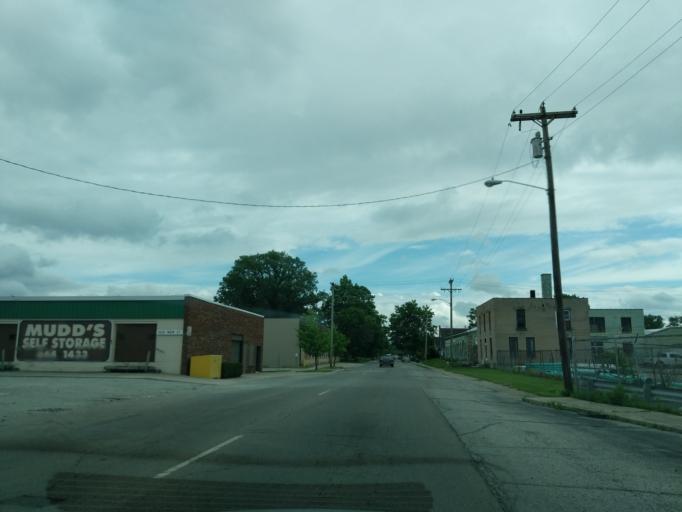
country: US
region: Indiana
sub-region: Madison County
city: Anderson
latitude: 40.1011
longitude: -85.6782
